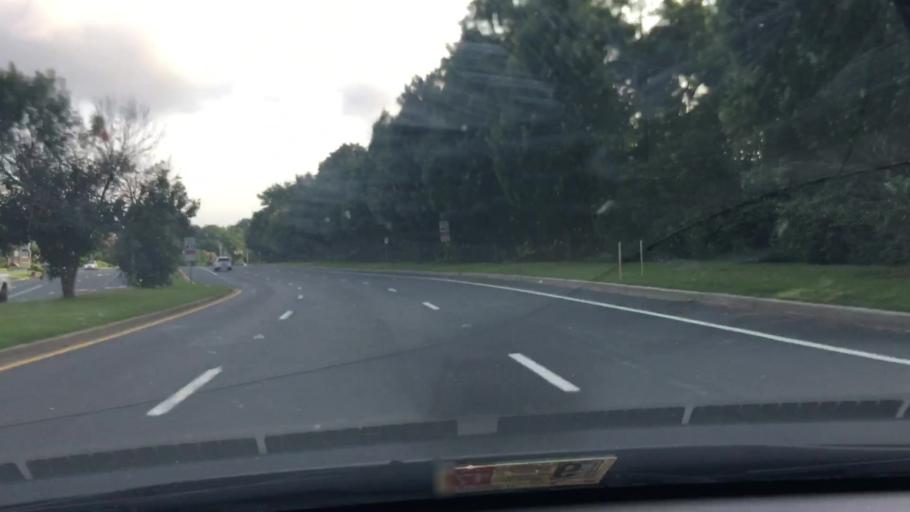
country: US
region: Maryland
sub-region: Montgomery County
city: Germantown
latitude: 39.1809
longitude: -77.2392
